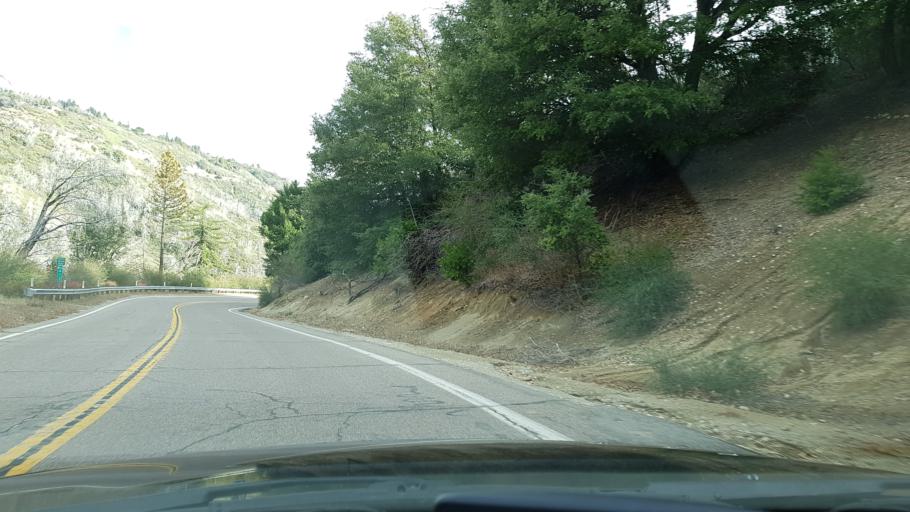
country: US
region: California
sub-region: Riverside County
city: Aguanga
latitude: 33.3117
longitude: -116.8720
